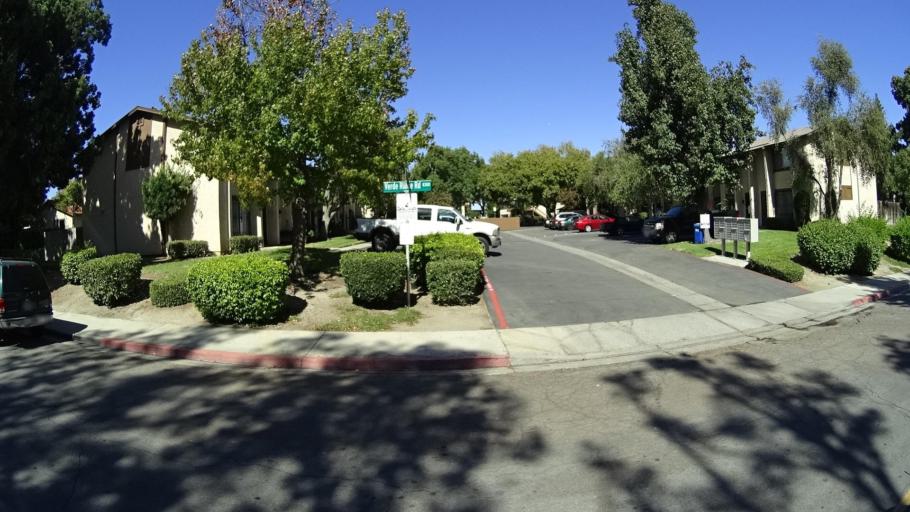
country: US
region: California
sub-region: San Diego County
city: La Presa
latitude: 32.6955
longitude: -117.0204
